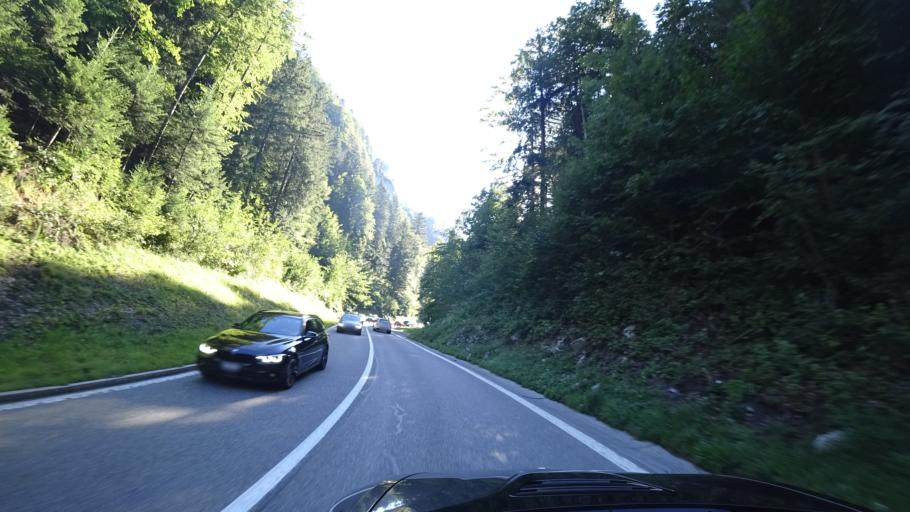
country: CH
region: Obwalden
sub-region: Obwalden
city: Lungern
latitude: 46.7757
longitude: 8.1497
